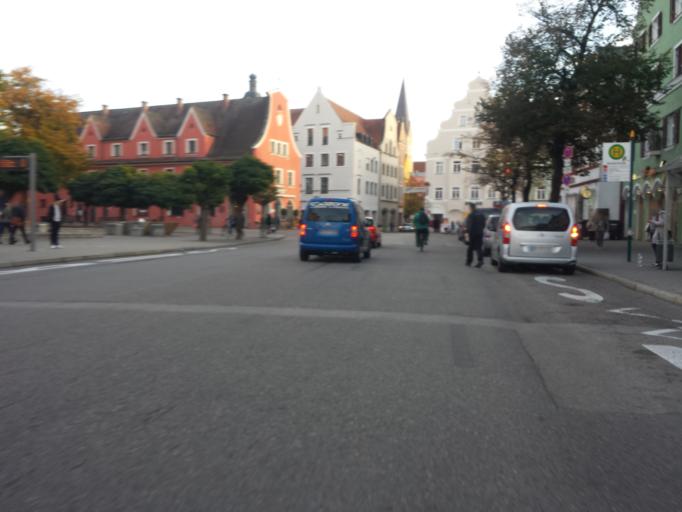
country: DE
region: Bavaria
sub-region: Upper Bavaria
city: Ingolstadt
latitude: 48.7658
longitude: 11.4232
